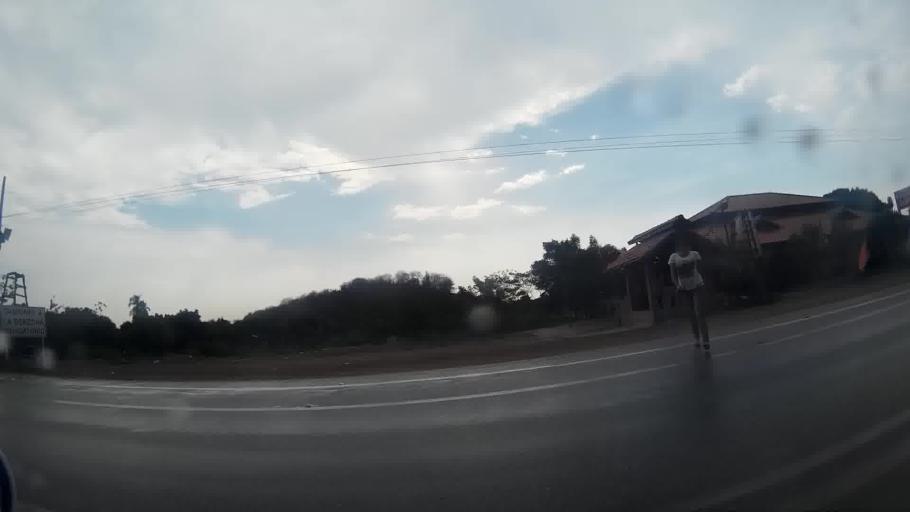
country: CO
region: Magdalena
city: Cienaga
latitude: 11.0153
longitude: -74.2149
